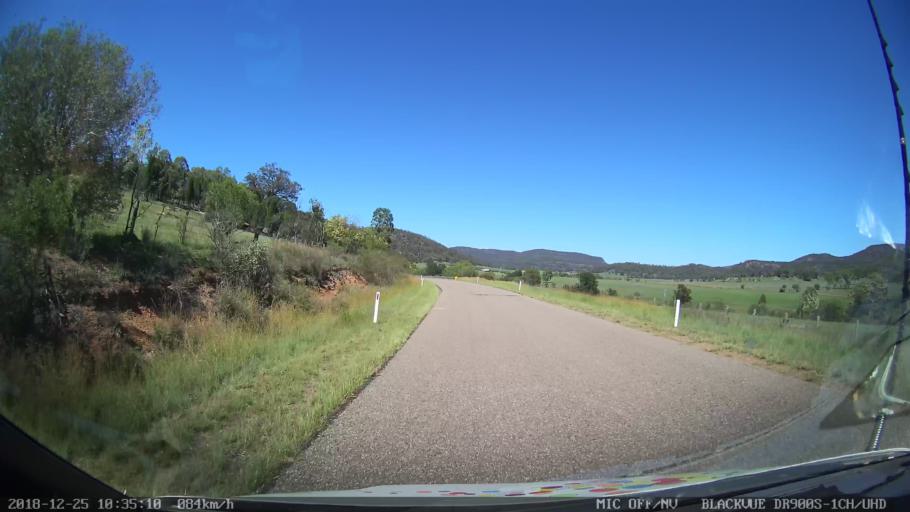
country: AU
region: New South Wales
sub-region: Upper Hunter Shire
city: Merriwa
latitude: -32.3958
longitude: 150.3985
